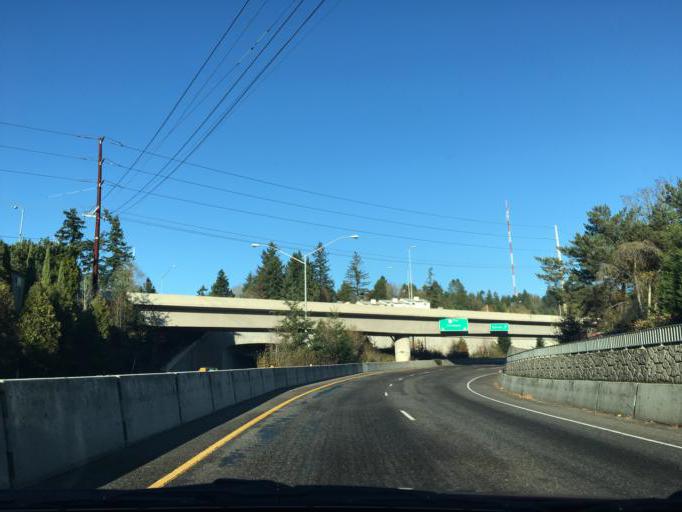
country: US
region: Oregon
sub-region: Washington County
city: West Slope
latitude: 45.5062
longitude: -122.7464
